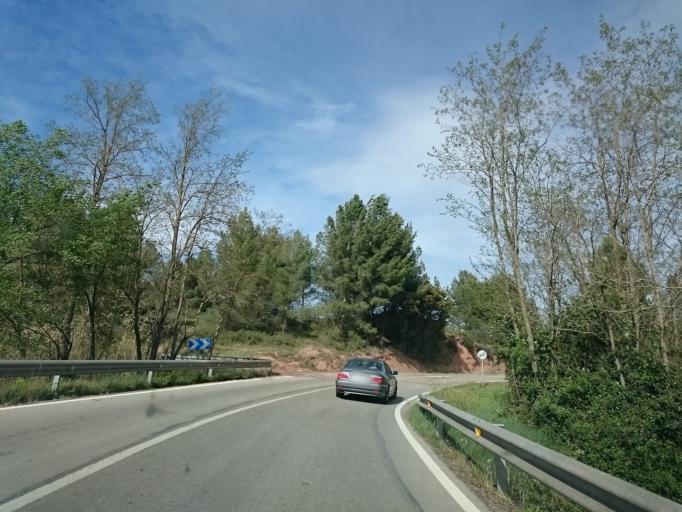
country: ES
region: Catalonia
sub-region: Provincia de Barcelona
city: Jorba
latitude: 41.5800
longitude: 1.5439
